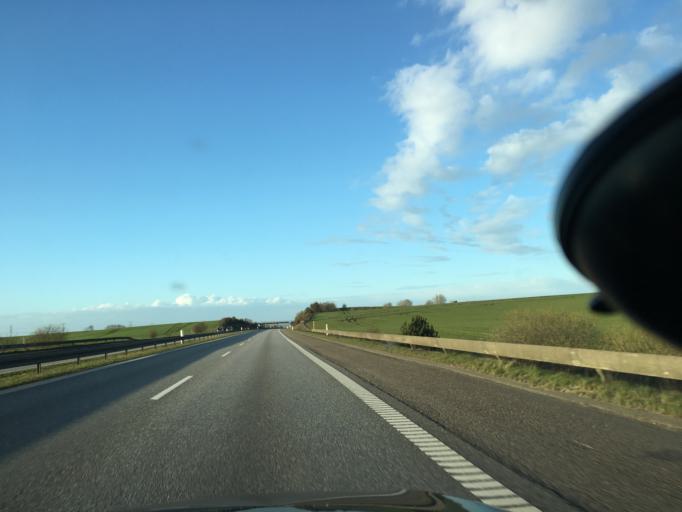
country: DK
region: North Denmark
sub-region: Alborg Kommune
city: Svenstrup
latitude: 56.9359
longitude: 9.8531
